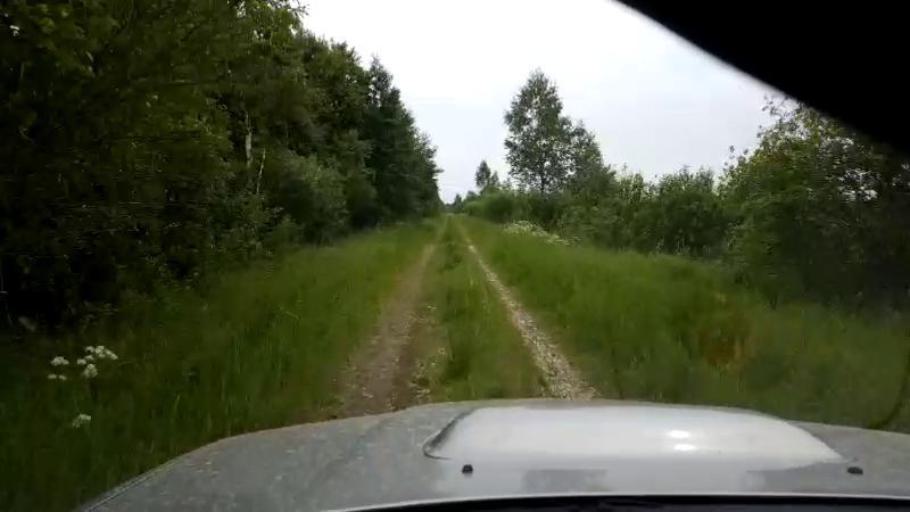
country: EE
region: Paernumaa
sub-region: Tootsi vald
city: Tootsi
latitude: 58.5653
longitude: 24.6891
